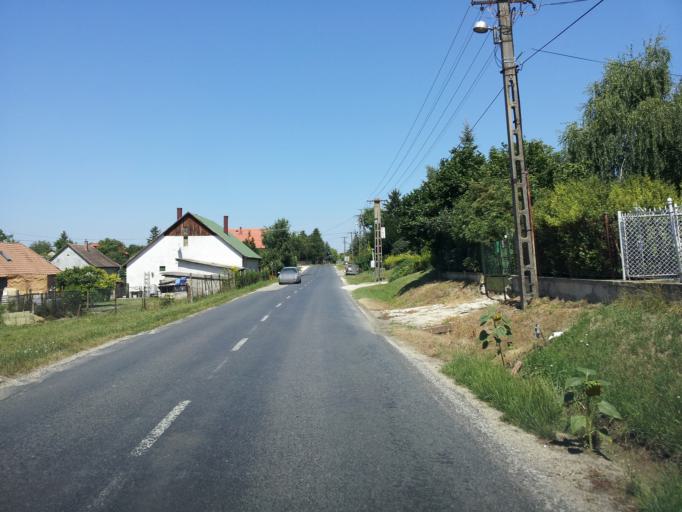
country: HU
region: Fejer
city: Lepseny
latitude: 47.0252
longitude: 18.2119
